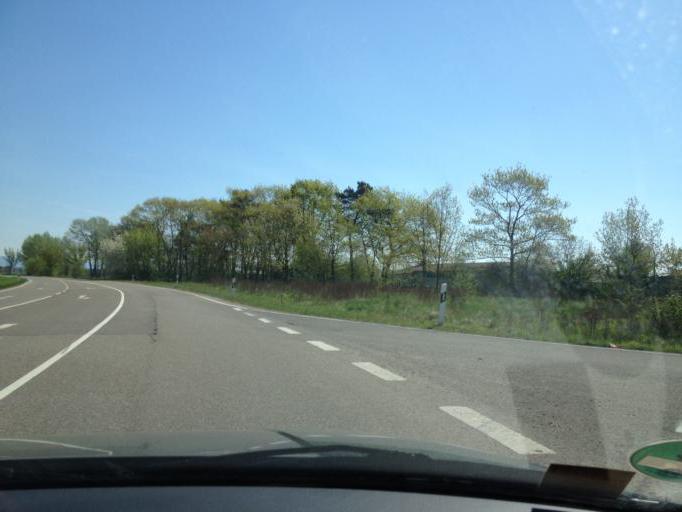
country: DE
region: Rheinland-Pfalz
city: Otterstadt
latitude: 49.3624
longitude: 8.4283
